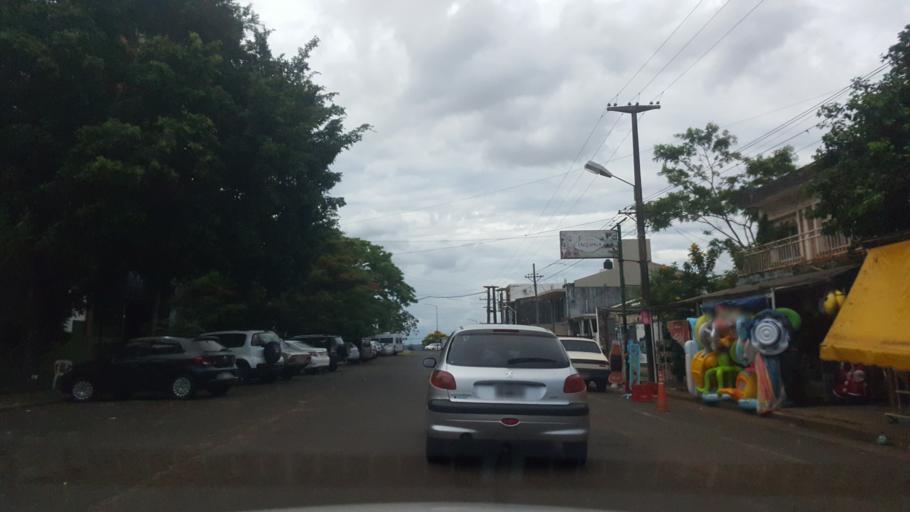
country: AR
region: Misiones
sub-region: Departamento de Capital
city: Posadas
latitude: -27.3649
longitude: -55.8867
